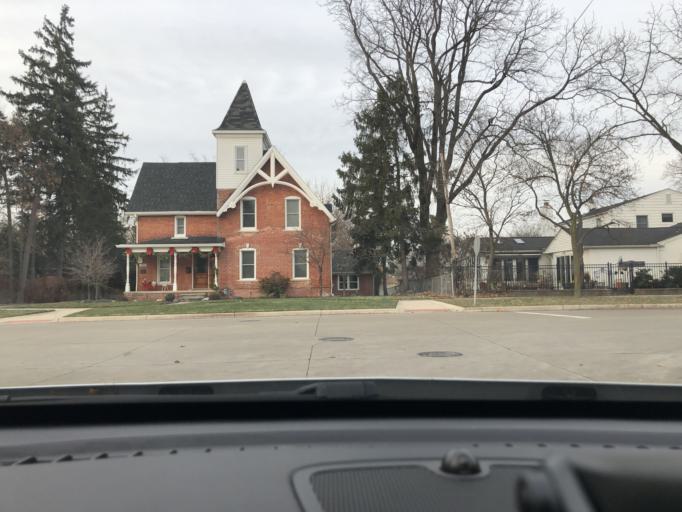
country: US
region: Michigan
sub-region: Wayne County
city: Dearborn Heights
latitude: 42.3078
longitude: -83.2469
